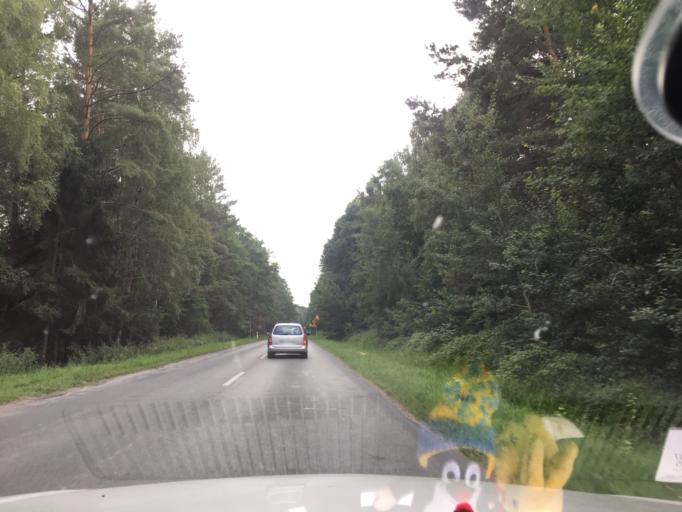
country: PL
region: West Pomeranian Voivodeship
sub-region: Powiat gryficki
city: Pobierowo
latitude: 54.0614
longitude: 14.9583
